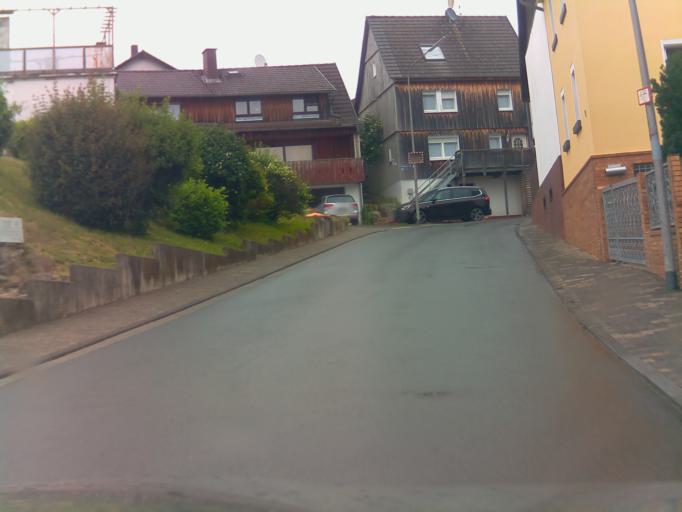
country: DE
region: Hesse
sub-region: Regierungsbezirk Darmstadt
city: Brensbach
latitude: 49.7799
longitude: 8.9377
